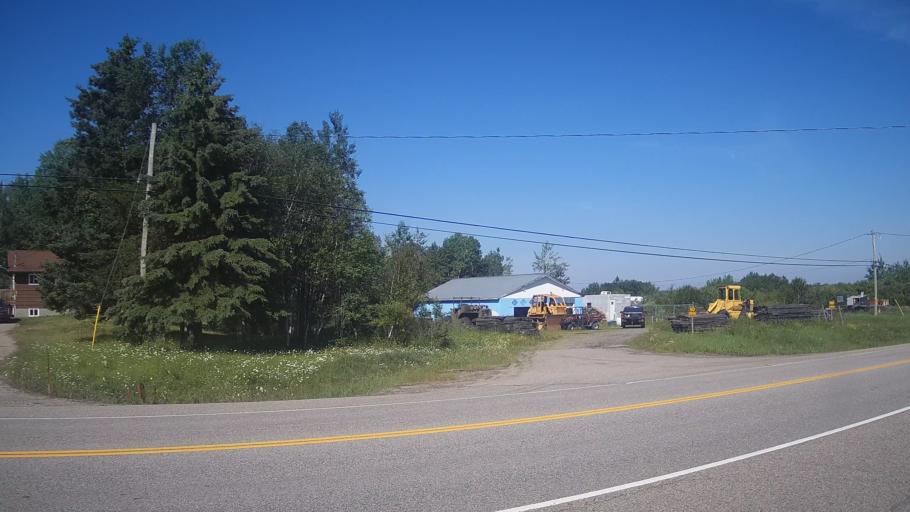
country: CA
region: Ontario
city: Dryden
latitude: 49.7341
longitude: -92.6129
